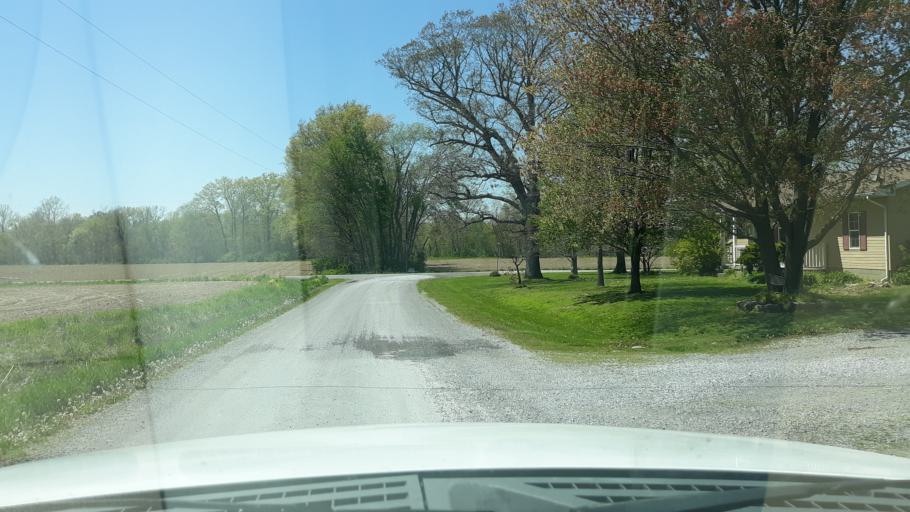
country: US
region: Illinois
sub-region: Saline County
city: Harrisburg
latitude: 37.8923
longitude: -88.6783
